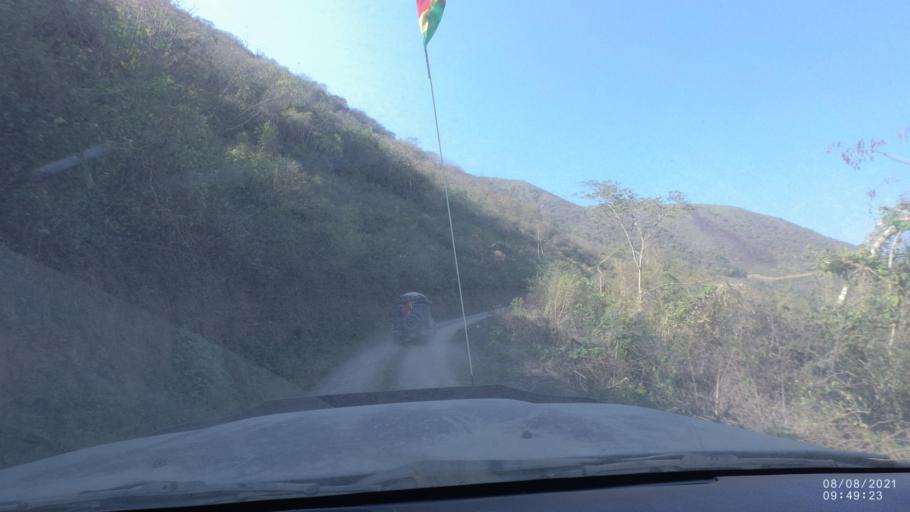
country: BO
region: La Paz
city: Quime
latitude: -16.6166
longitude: -66.7289
